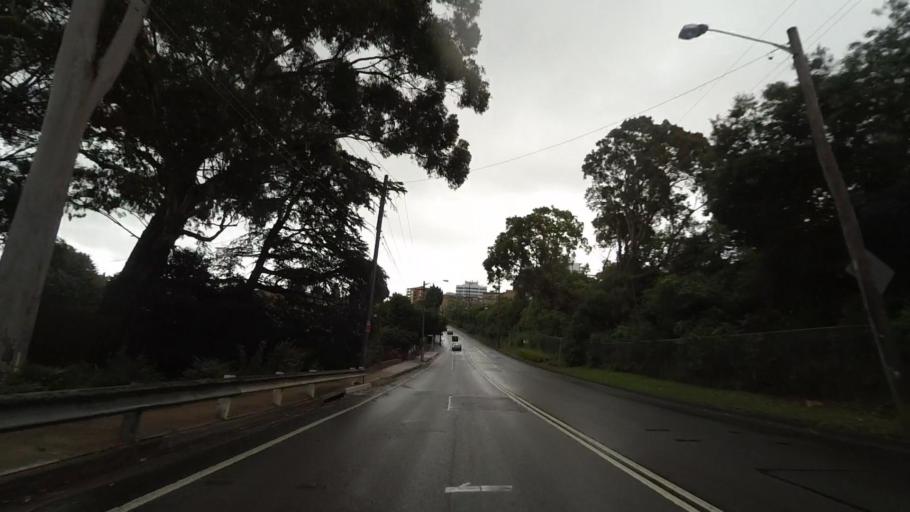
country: AU
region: New South Wales
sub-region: Hurstville
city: Penshurst
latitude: -33.9660
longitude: 151.0992
